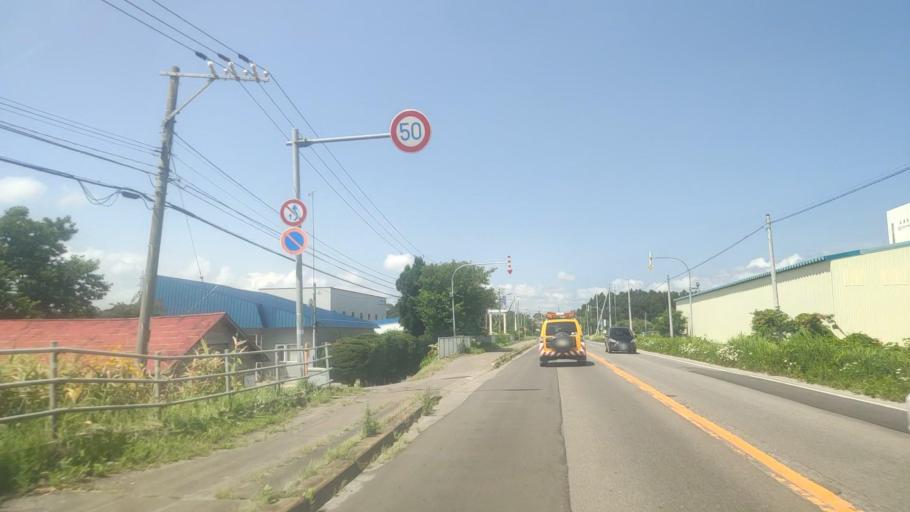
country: JP
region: Hokkaido
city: Nanae
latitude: 42.2397
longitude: 140.3004
